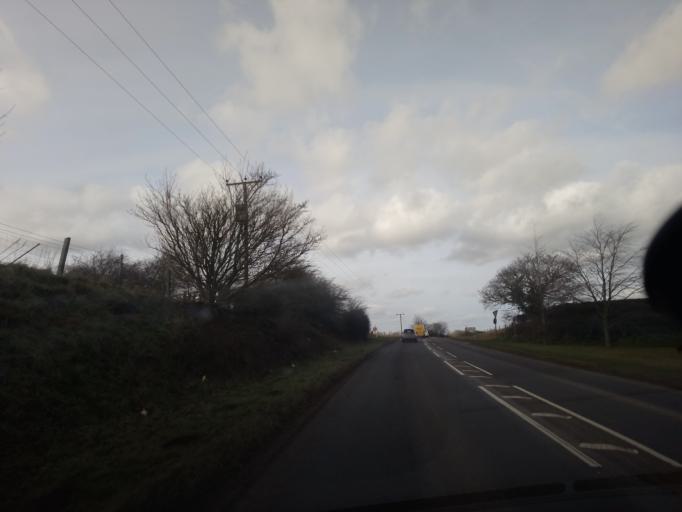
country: GB
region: England
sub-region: Telford and Wrekin
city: Eyton upon the Weald Moors
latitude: 52.7742
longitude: -2.5518
